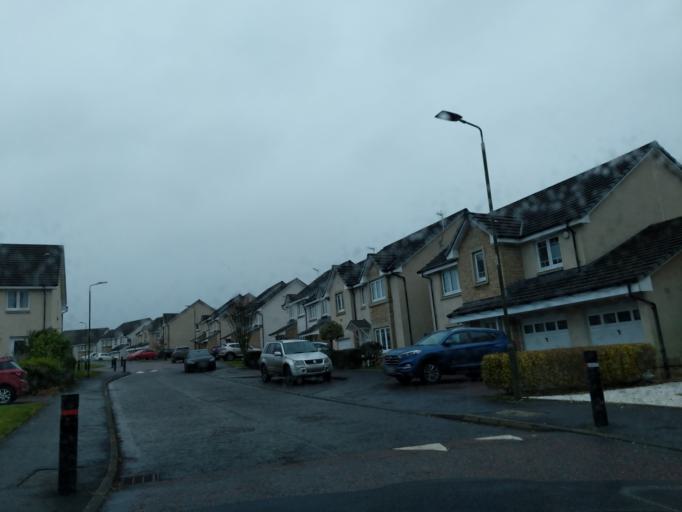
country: GB
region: Scotland
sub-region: Falkirk
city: Falkirk
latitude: 55.9849
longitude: -3.7915
